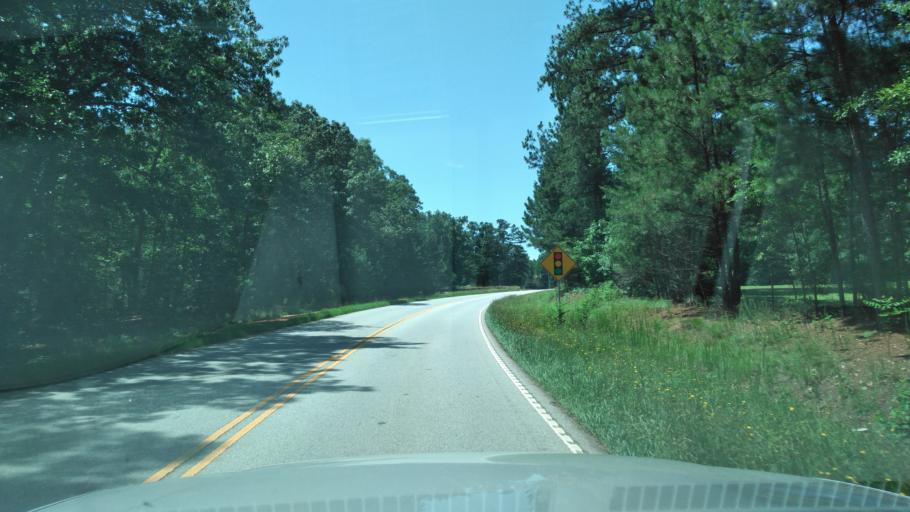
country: US
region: South Carolina
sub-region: Laurens County
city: Laurens
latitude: 34.4951
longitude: -82.0551
